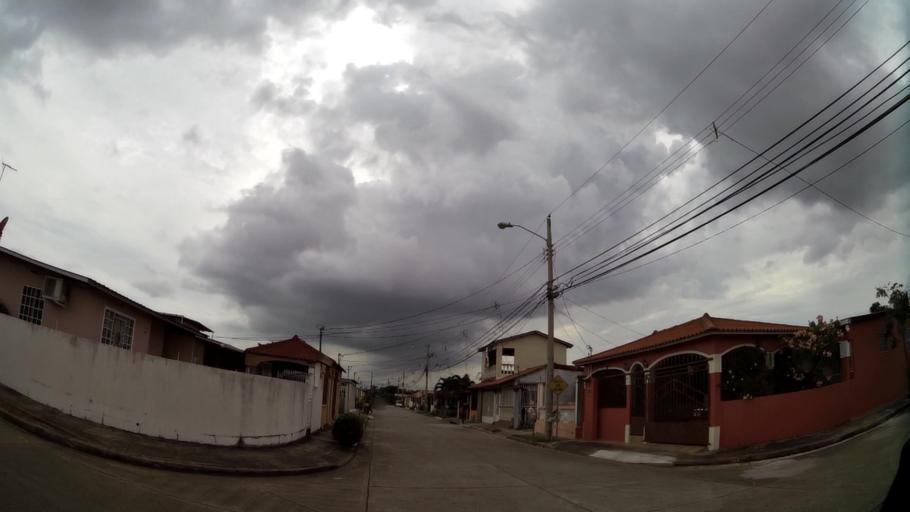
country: PA
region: Panama
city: Tocumen
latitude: 9.0513
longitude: -79.4106
